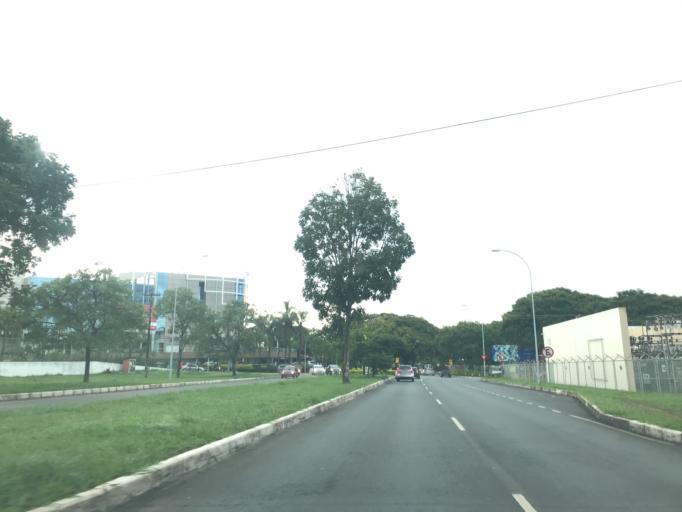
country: BR
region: Federal District
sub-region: Brasilia
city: Brasilia
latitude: -15.8133
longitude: -47.9149
